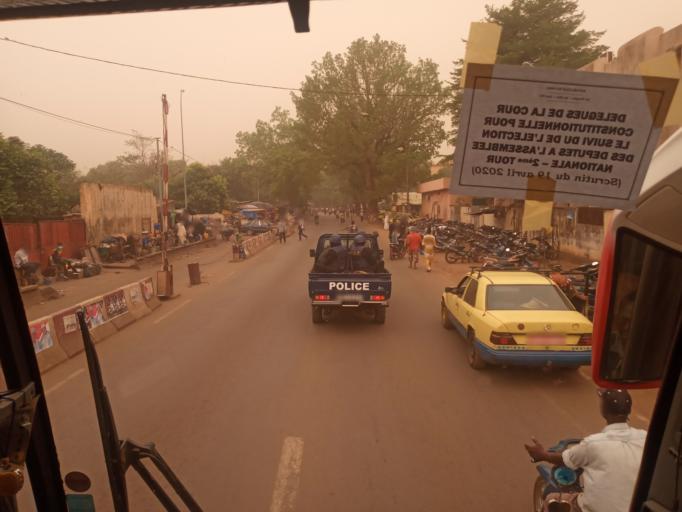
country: ML
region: Bamako
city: Bamako
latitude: 12.6510
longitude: -7.9937
